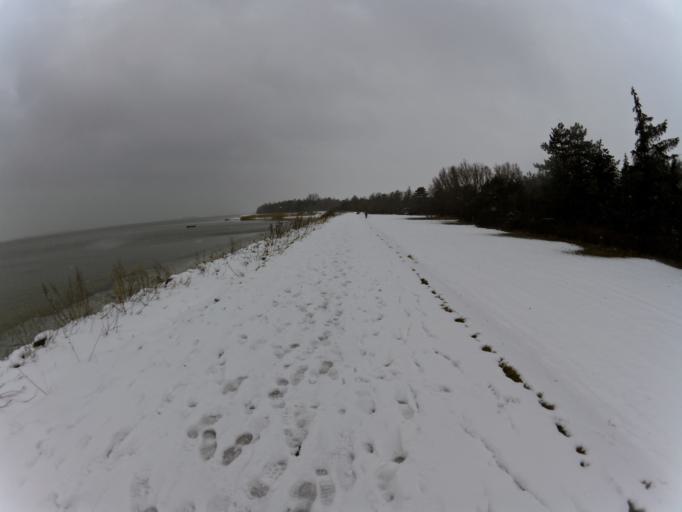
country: DK
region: Zealand
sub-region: Vordingborg Kommune
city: Neder Vindinge
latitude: 55.0527
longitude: 11.8310
